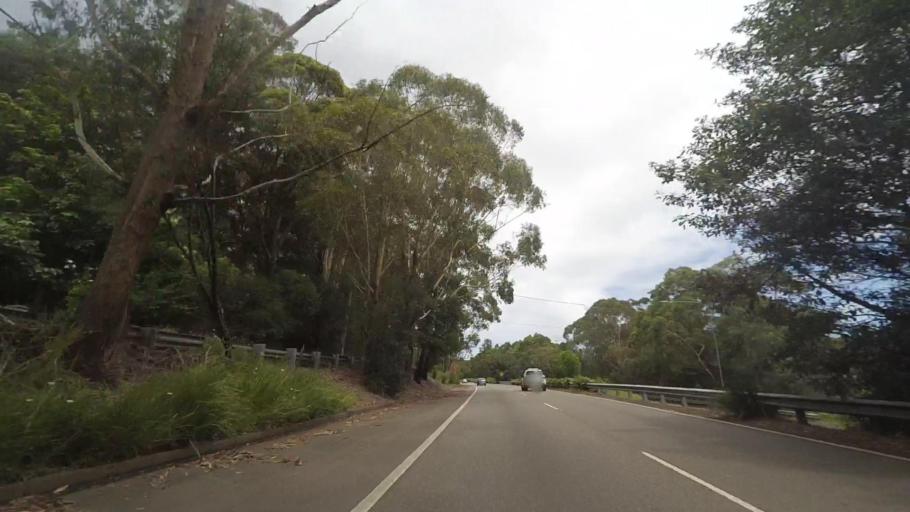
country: AU
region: New South Wales
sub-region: Wyong Shire
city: Berkeley Vale
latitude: -33.3492
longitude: 151.4317
